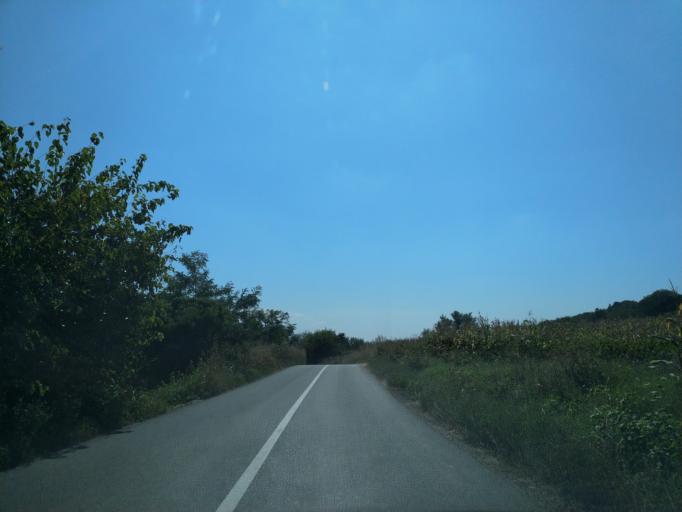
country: RS
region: Central Serbia
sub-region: Rasinski Okrug
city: Krusevac
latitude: 43.6333
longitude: 21.3728
